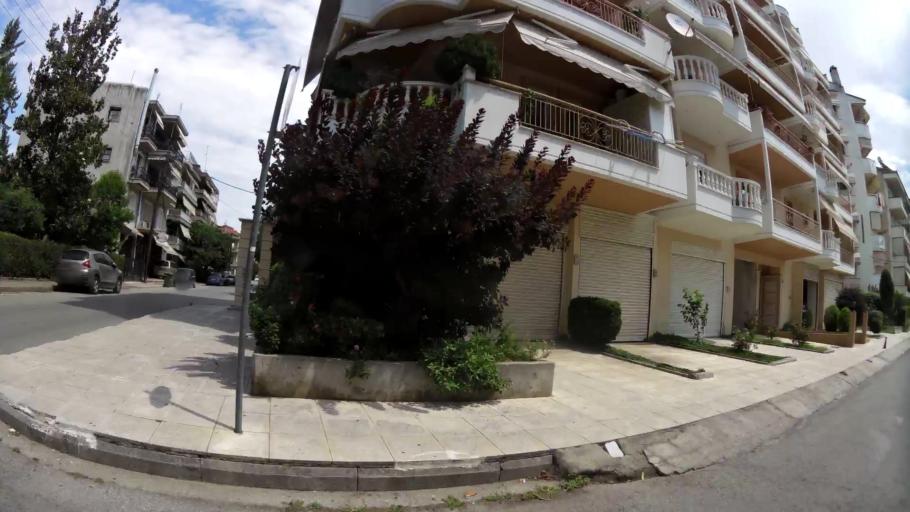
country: GR
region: Central Macedonia
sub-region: Nomos Pierias
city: Katerini
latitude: 40.2689
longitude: 22.5032
